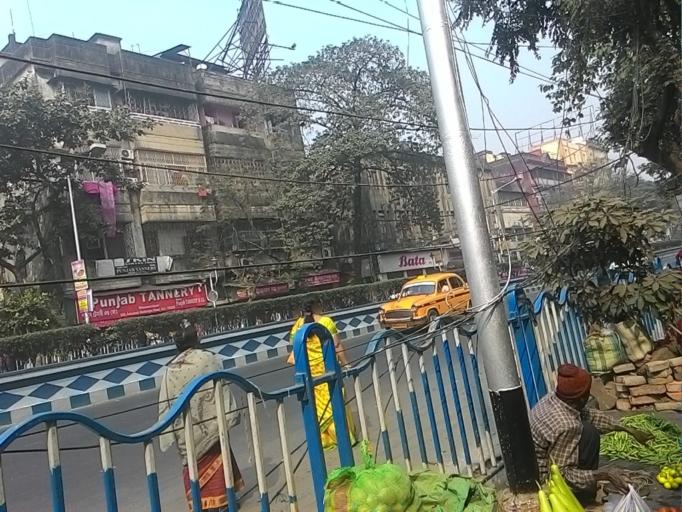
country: IN
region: West Bengal
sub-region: Kolkata
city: Bara Bazar
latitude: 22.5319
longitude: 88.3460
